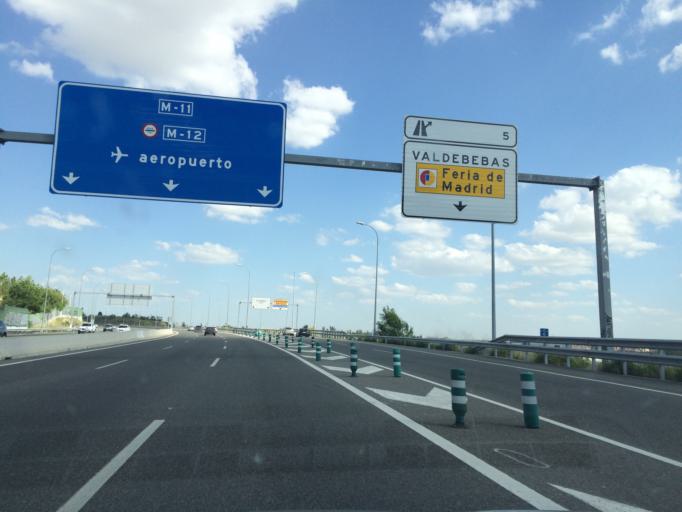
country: ES
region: Madrid
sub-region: Provincia de Madrid
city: Hortaleza
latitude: 40.4748
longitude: -3.6299
